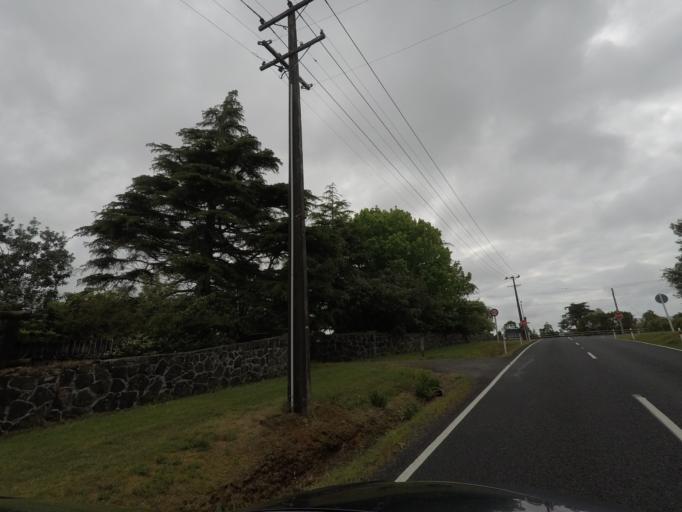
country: NZ
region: Auckland
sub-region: Auckland
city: Rosebank
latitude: -36.8225
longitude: 174.5772
